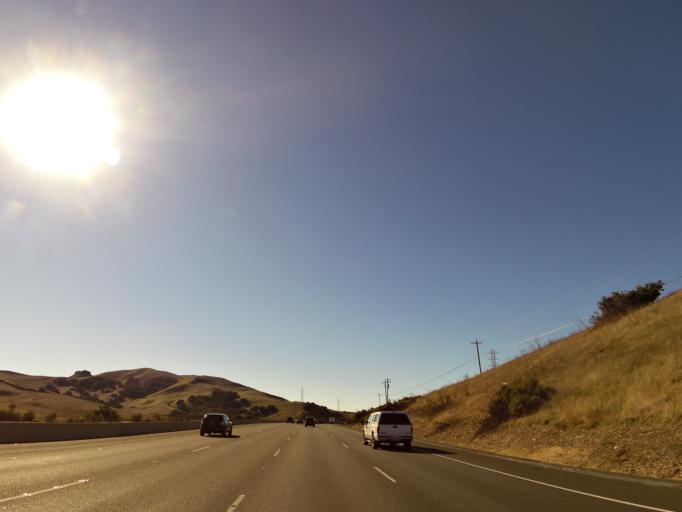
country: US
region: California
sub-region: Solano County
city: Green Valley
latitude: 38.1918
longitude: -122.1682
